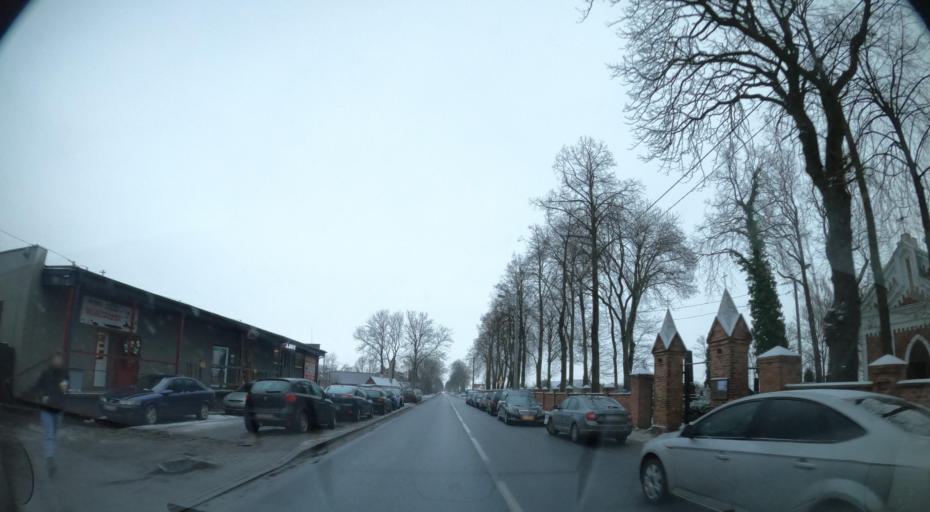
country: PL
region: Kujawsko-Pomorskie
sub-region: Powiat lipnowski
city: Dobrzyn nad Wisla
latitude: 52.6402
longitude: 19.3184
